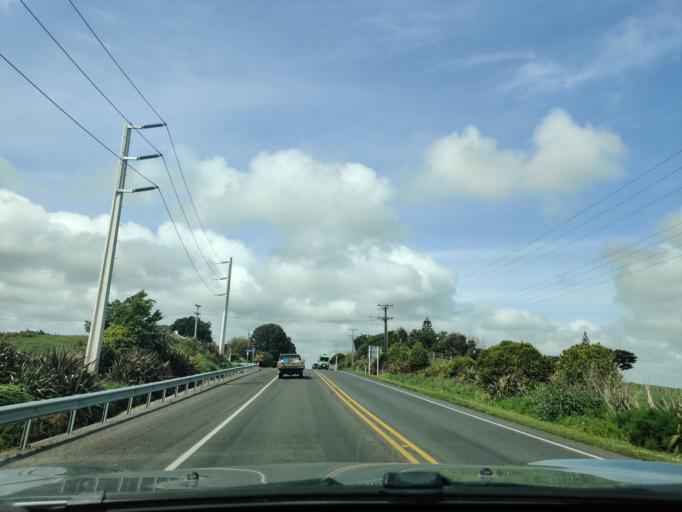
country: NZ
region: Taranaki
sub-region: South Taranaki District
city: Patea
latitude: -39.7649
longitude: 174.6230
